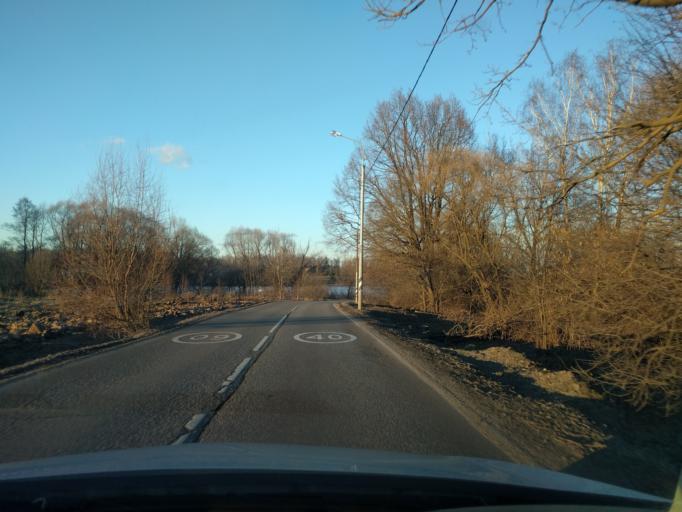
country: RU
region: Moskovskaya
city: Vatutinki
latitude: 55.4876
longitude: 37.4076
